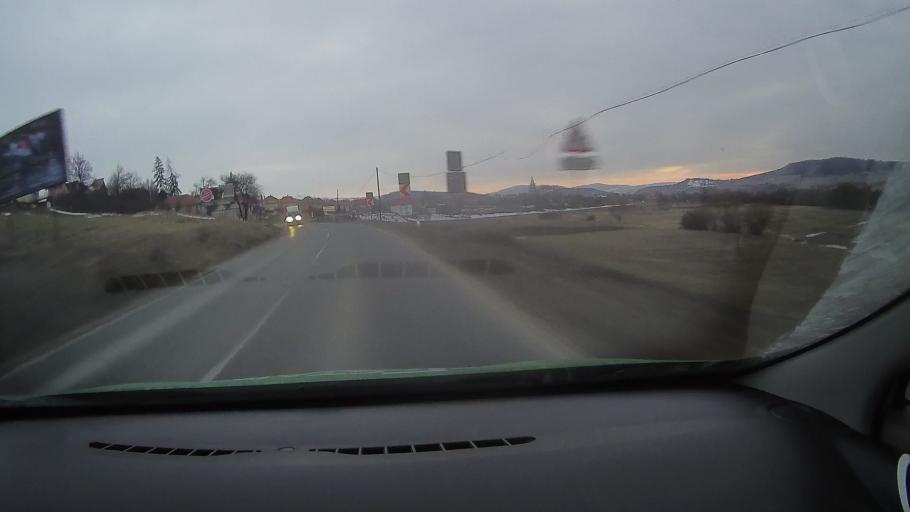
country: RO
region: Harghita
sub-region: Comuna Feliceni
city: Feliceni
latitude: 46.2775
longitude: 25.2860
